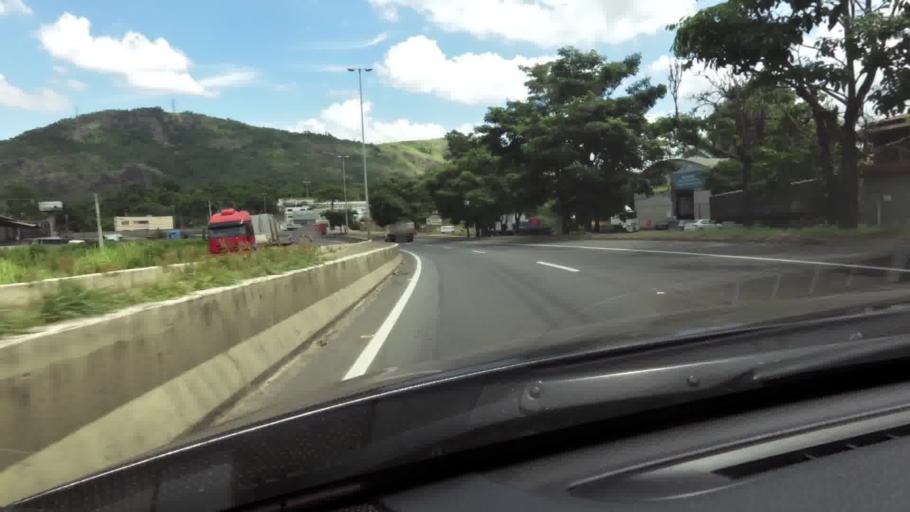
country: BR
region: Espirito Santo
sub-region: Viana
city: Viana
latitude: -20.3832
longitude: -40.4603
